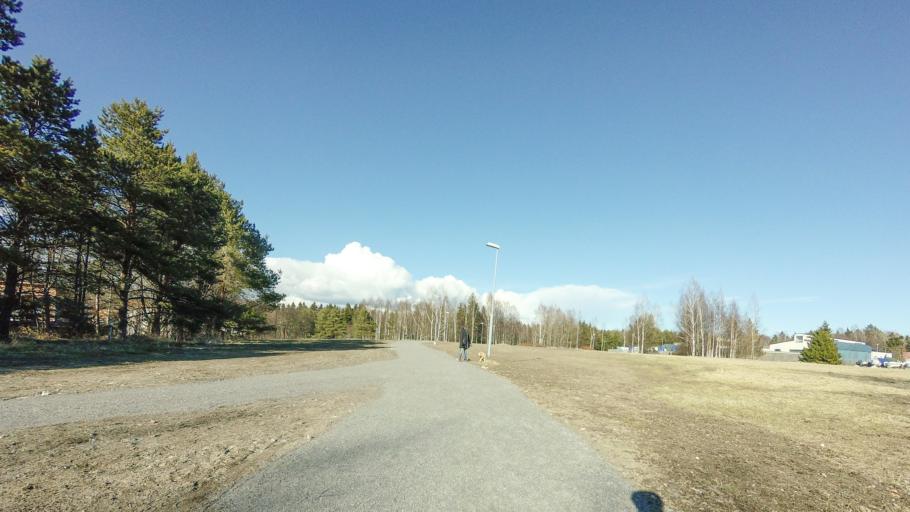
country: FI
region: Uusimaa
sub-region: Helsinki
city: Helsinki
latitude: 60.1690
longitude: 25.0561
